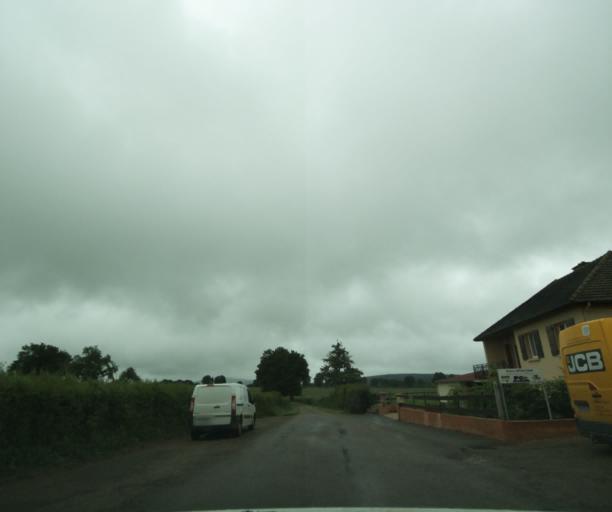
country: FR
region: Bourgogne
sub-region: Departement de Saone-et-Loire
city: Charolles
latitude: 46.4312
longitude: 4.3239
